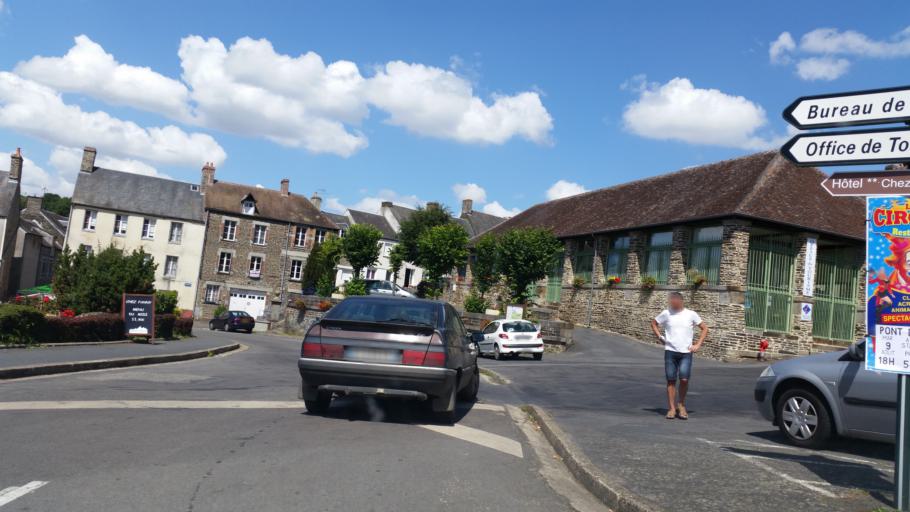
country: FR
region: Lower Normandy
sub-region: Departement du Calvados
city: Clecy
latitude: 48.8736
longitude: -0.4081
